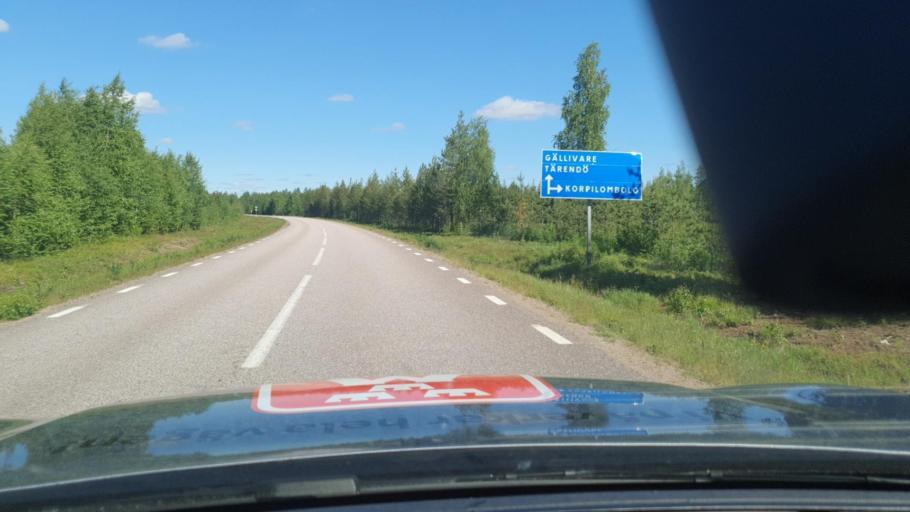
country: SE
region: Norrbotten
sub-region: Overkalix Kommun
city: OEverkalix
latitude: 66.9071
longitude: 22.7758
